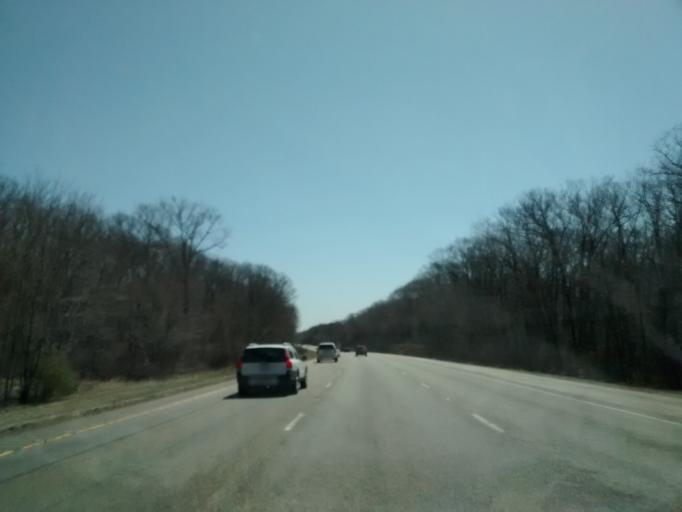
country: US
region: Massachusetts
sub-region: Middlesex County
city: Hopkinton
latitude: 42.1864
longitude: -71.5340
